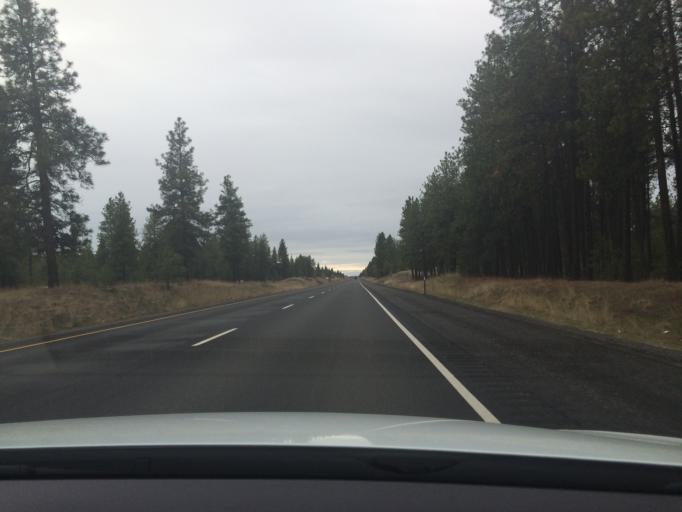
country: US
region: Washington
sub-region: Spokane County
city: Medical Lake
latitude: 47.4771
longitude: -117.7311
